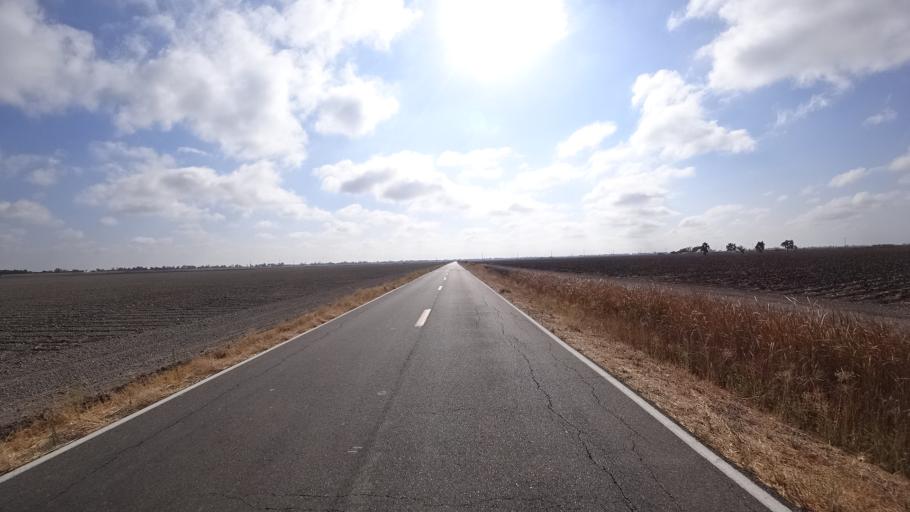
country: US
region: California
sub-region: Yolo County
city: Woodland
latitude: 38.8321
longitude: -121.7509
